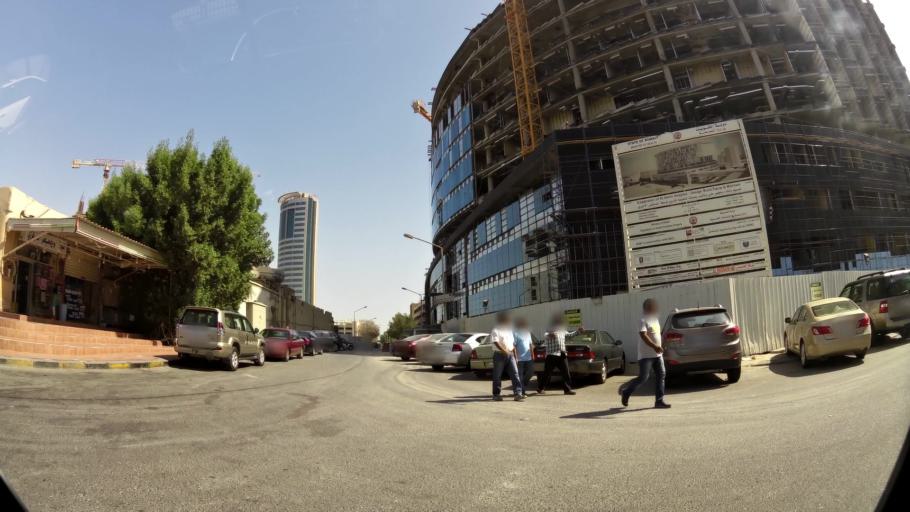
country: KW
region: Al Asimah
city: Kuwait City
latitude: 29.3883
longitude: 47.9880
